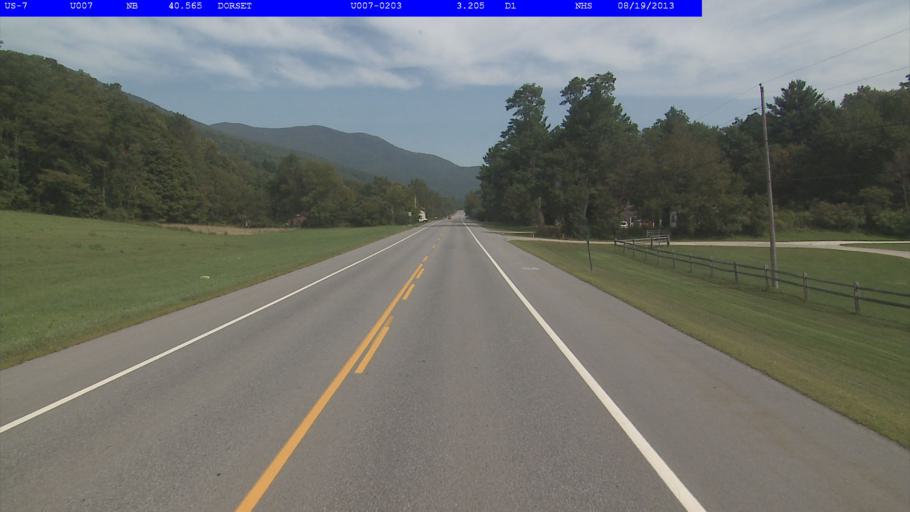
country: US
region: Vermont
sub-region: Bennington County
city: Manchester Center
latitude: 43.2553
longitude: -73.0079
